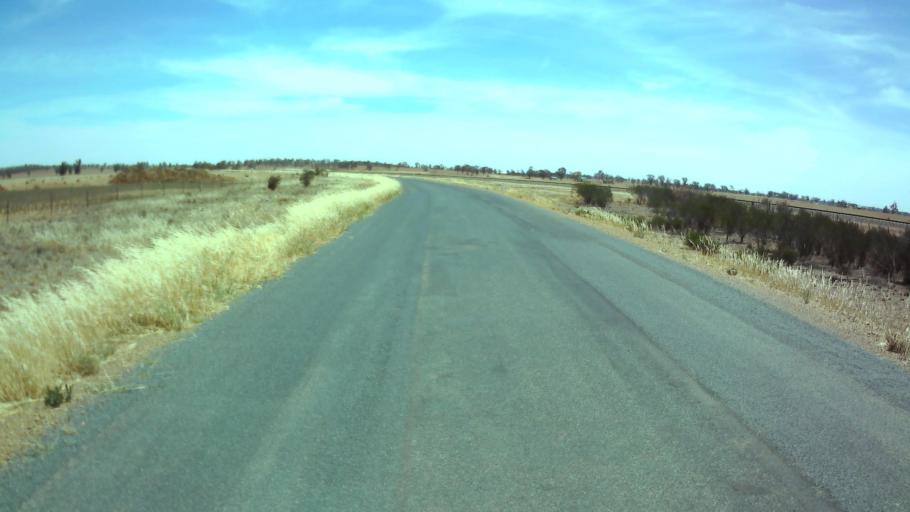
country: AU
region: New South Wales
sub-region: Weddin
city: Grenfell
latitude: -33.7539
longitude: 147.7646
